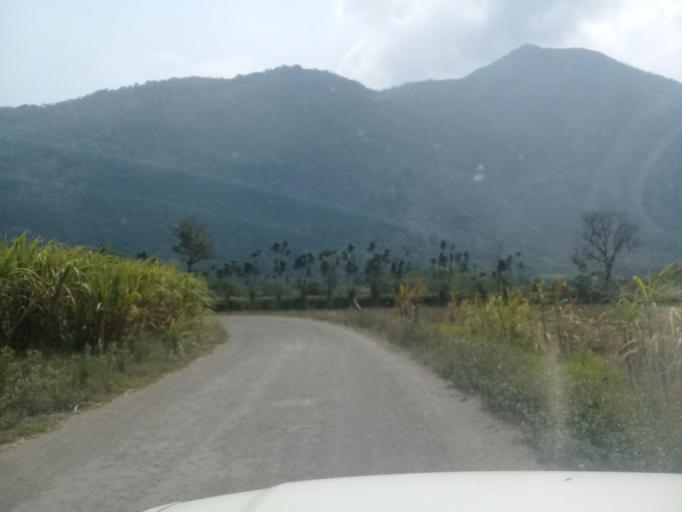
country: MX
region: Veracruz
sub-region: Ixtaczoquitlan
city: Capoluca
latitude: 18.8114
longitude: -96.9896
